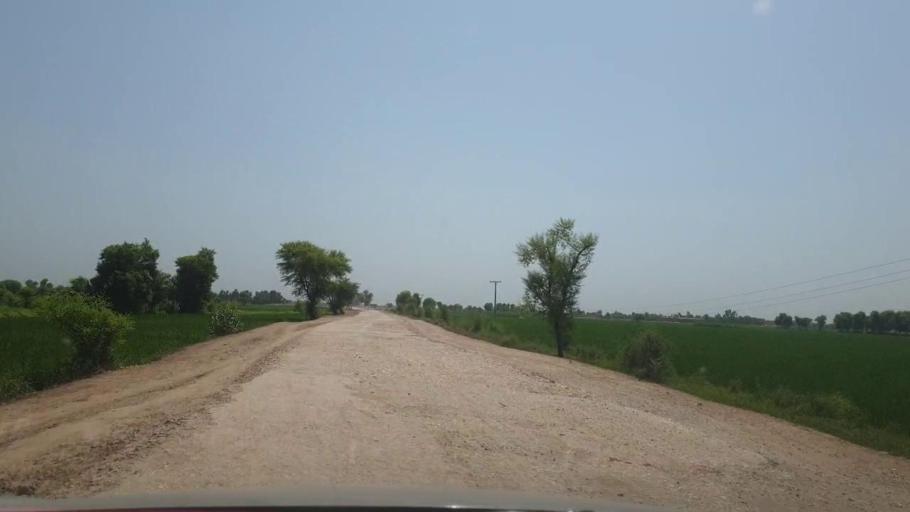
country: PK
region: Sindh
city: Warah
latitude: 27.5060
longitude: 67.7931
